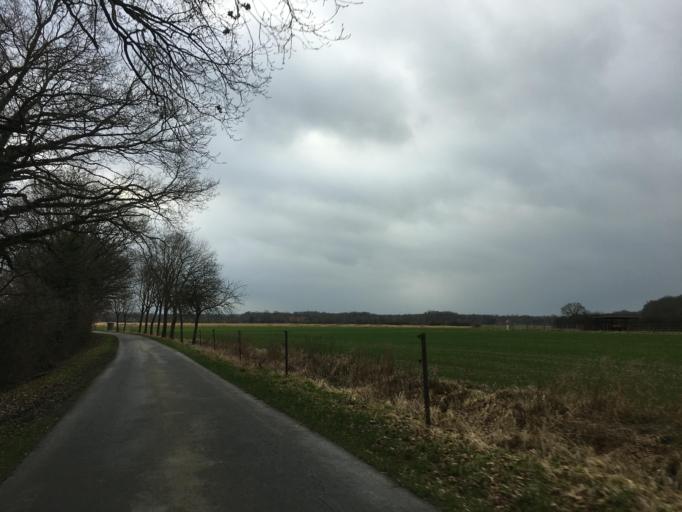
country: DE
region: North Rhine-Westphalia
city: Ludinghausen
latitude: 51.7976
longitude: 7.4575
